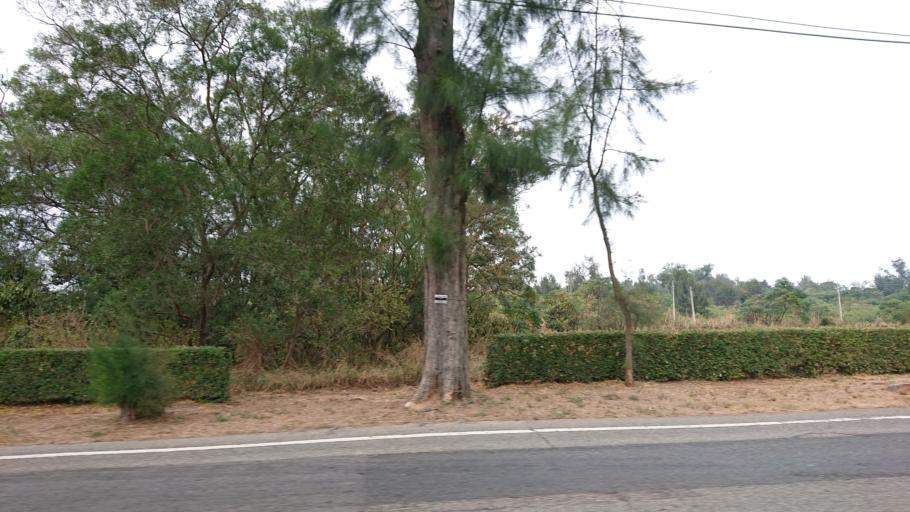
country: TW
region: Fukien
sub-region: Kinmen
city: Jincheng
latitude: 24.4512
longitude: 118.3459
